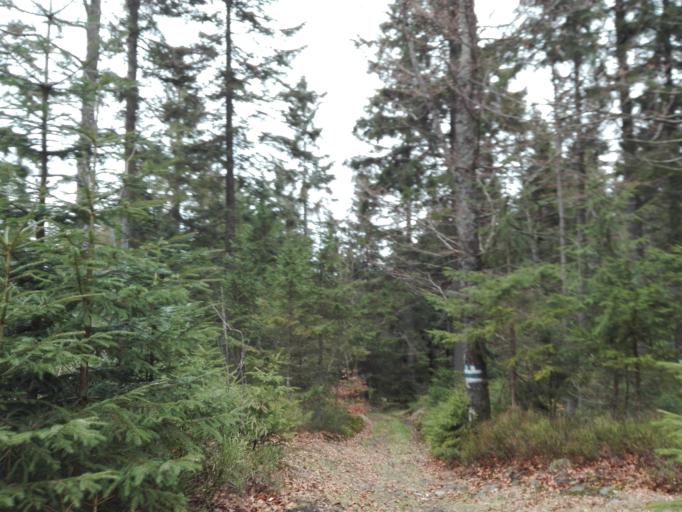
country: AT
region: Upper Austria
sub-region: Politischer Bezirk Rohrbach
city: Ulrichsberg
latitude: 48.6990
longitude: 13.9548
